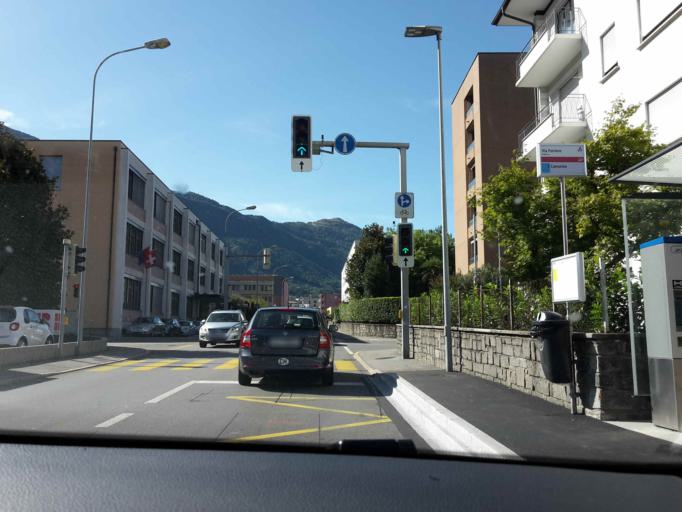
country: CH
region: Ticino
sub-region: Bellinzona District
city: Giubiasco
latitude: 46.1762
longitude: 9.0125
